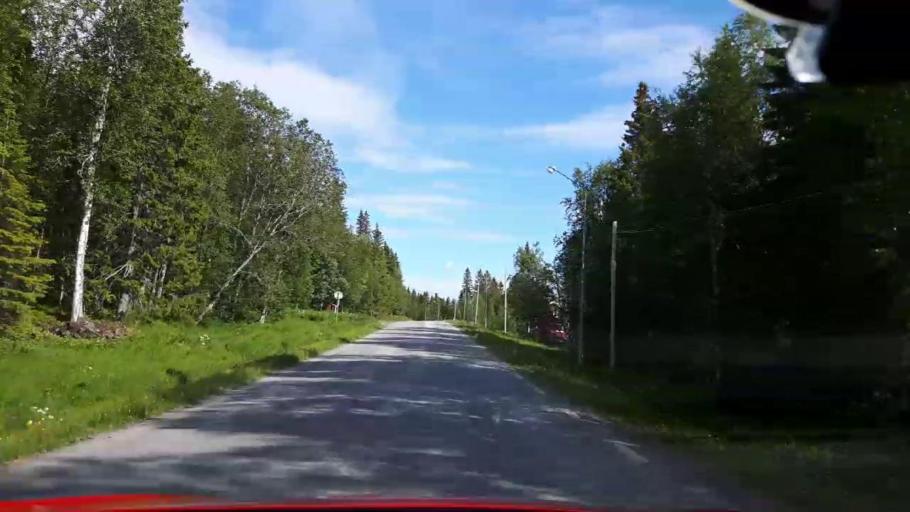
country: SE
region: Jaemtland
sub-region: Krokoms Kommun
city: Valla
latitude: 63.7704
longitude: 14.0534
